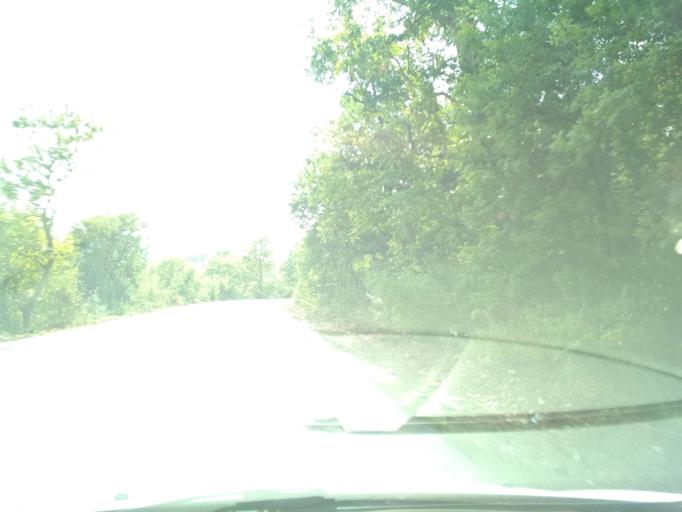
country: GR
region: Central Greece
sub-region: Nomos Evvoias
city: Prokopion
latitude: 38.7296
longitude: 23.5013
